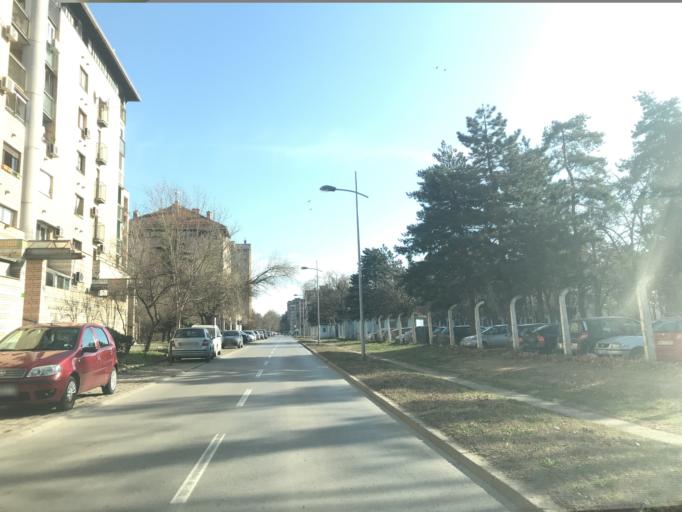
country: RS
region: Autonomna Pokrajina Vojvodina
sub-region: Juznobacki Okrug
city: Novi Sad
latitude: 45.2354
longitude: 19.8280
